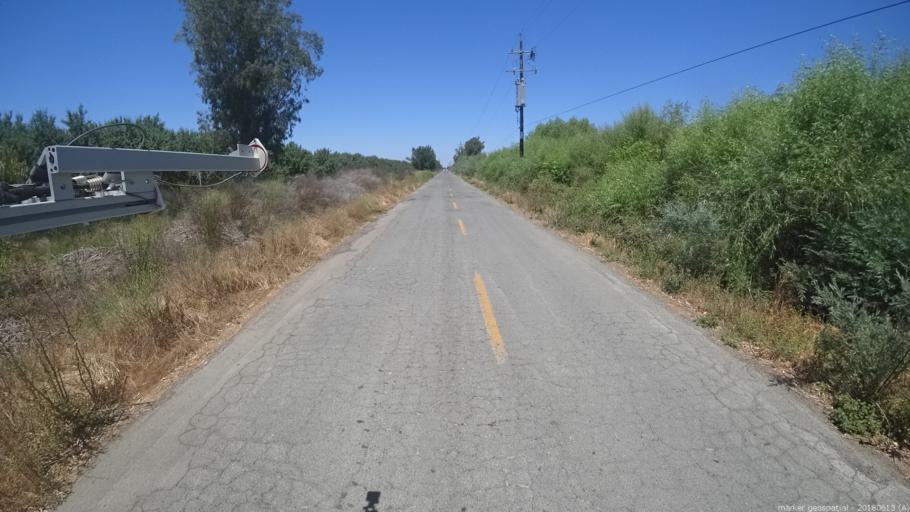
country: US
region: California
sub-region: Madera County
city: Fairmead
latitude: 36.9989
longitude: -120.2742
